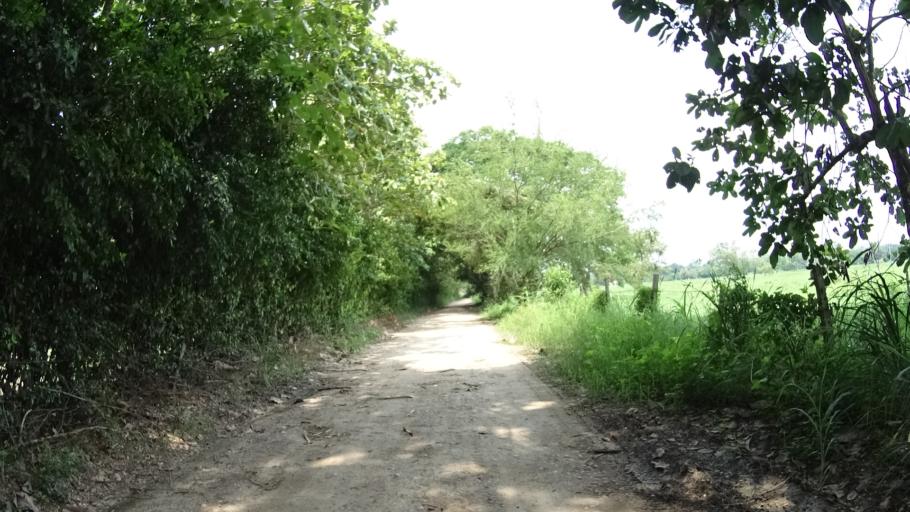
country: CO
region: Cundinamarca
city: Puerto Salgar
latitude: 5.5395
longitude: -74.6765
